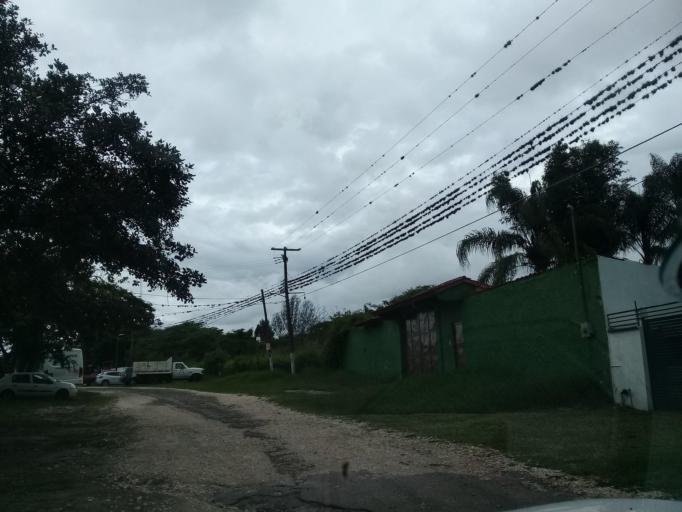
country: MX
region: Veracruz
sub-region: Emiliano Zapata
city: Dos Rios
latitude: 19.4827
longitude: -96.7948
